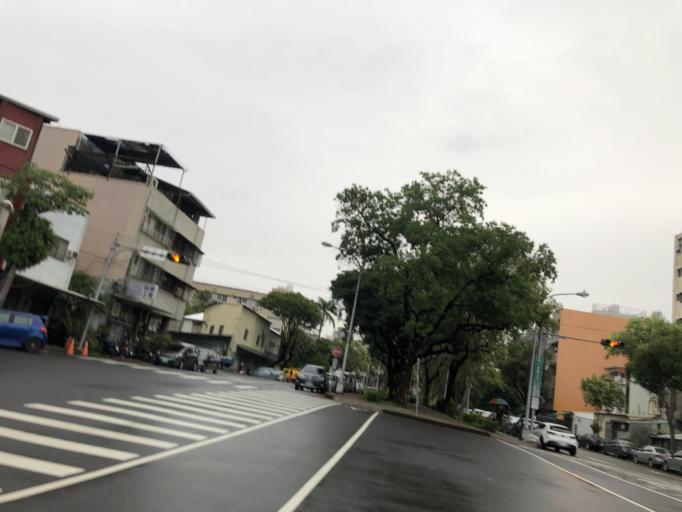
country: TW
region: Taiwan
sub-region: Taichung City
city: Taichung
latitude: 24.1529
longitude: 120.6732
